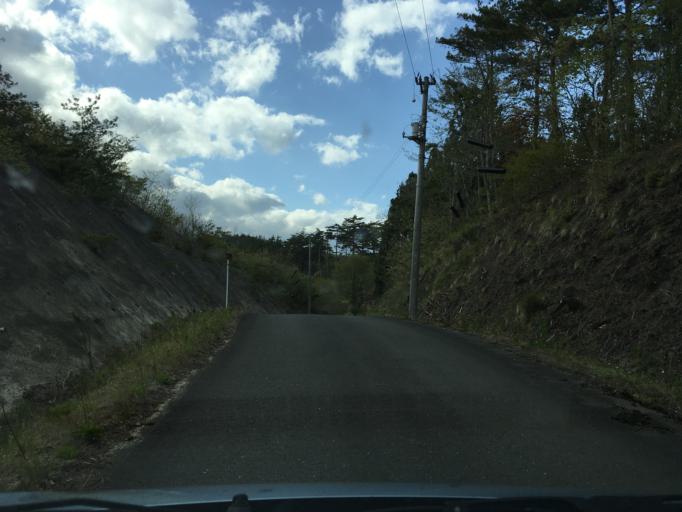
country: JP
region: Iwate
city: Ichinoseki
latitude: 38.7991
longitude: 141.4125
